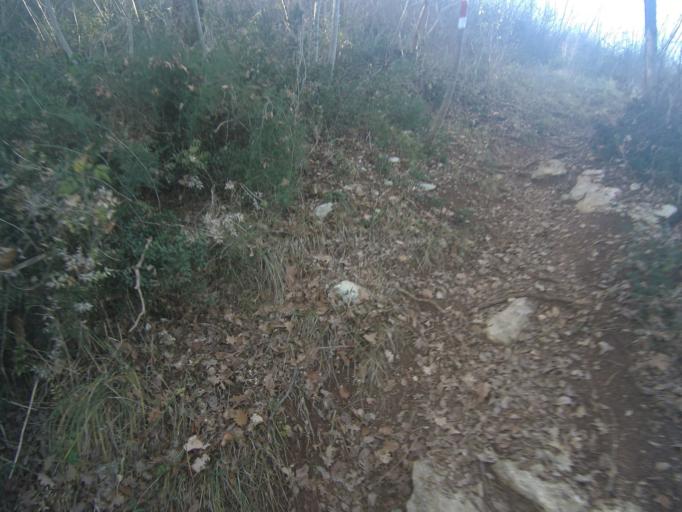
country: IT
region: Veneto
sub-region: Provincia di Vicenza
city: Lumignano
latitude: 45.4521
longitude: 11.5788
